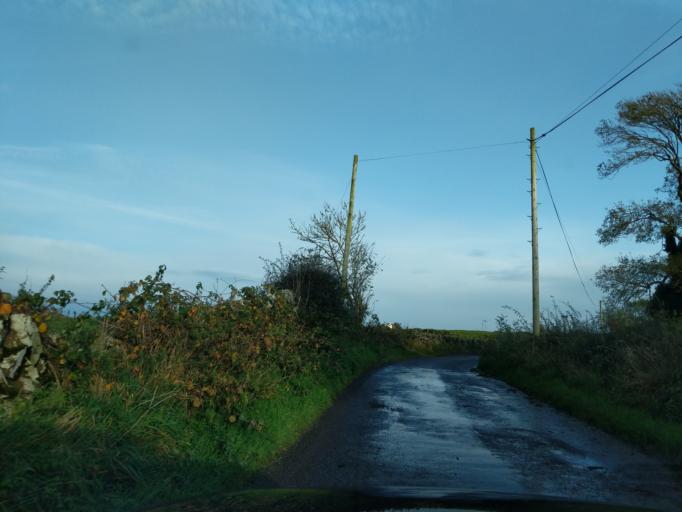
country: GB
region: Scotland
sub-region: Dumfries and Galloway
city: Kirkcudbright
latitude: 54.8124
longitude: -4.1664
